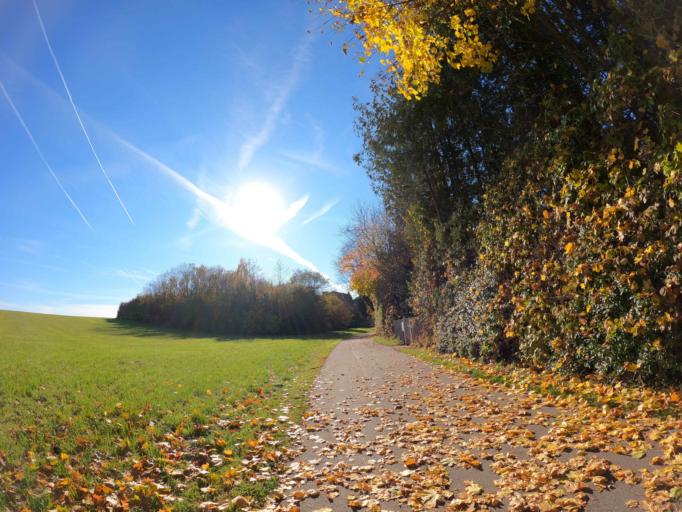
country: DE
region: Bavaria
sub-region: Upper Bavaria
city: Oberhaching
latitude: 48.0259
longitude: 11.6019
